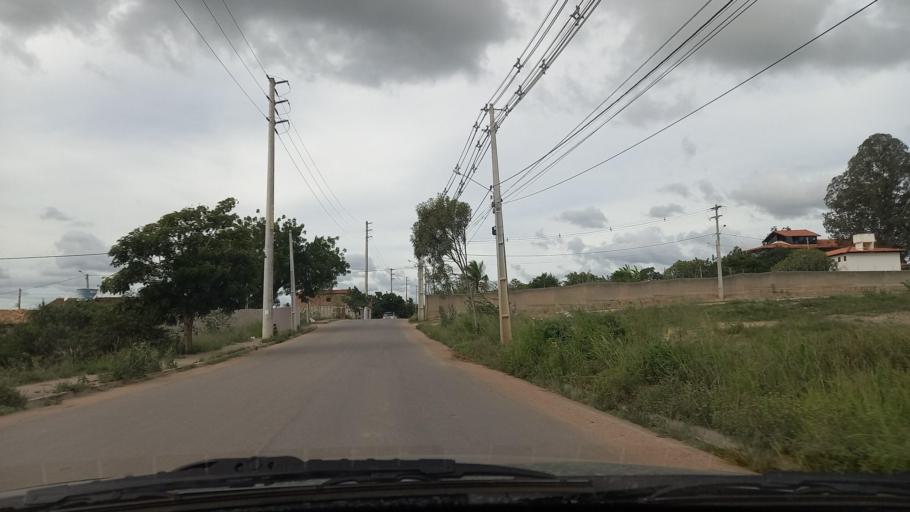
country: BR
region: Pernambuco
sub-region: Gravata
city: Gravata
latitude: -8.2017
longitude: -35.5469
